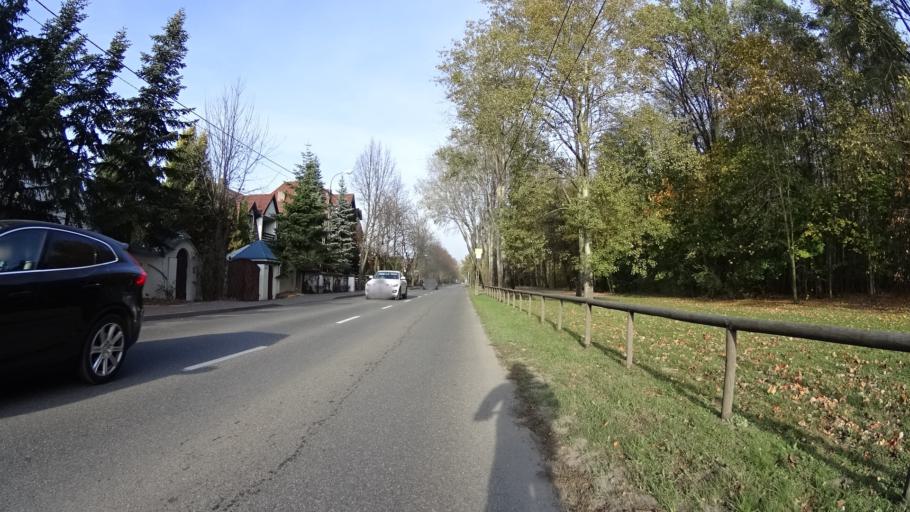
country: PL
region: Masovian Voivodeship
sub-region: Powiat warszawski zachodni
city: Babice
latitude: 52.2606
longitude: 20.8536
